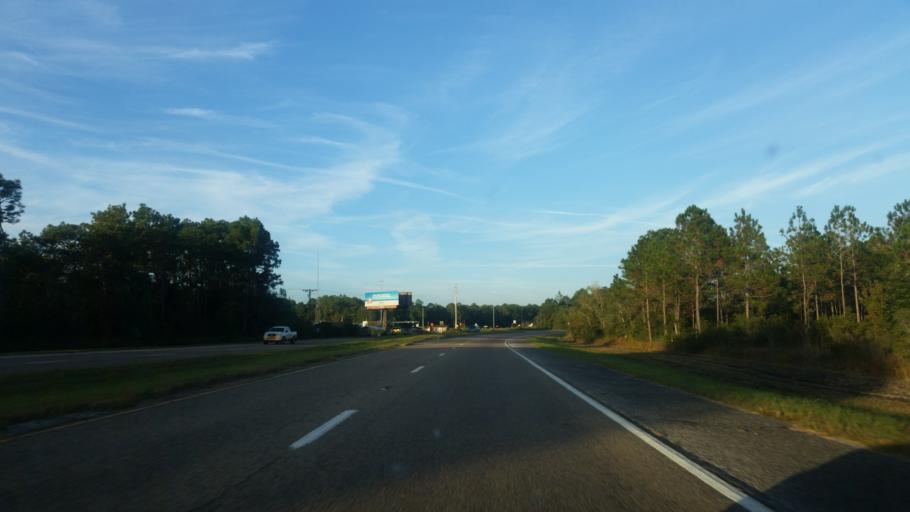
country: US
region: Alabama
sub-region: Mobile County
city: Grand Bay
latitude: 30.4697
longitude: -88.4063
